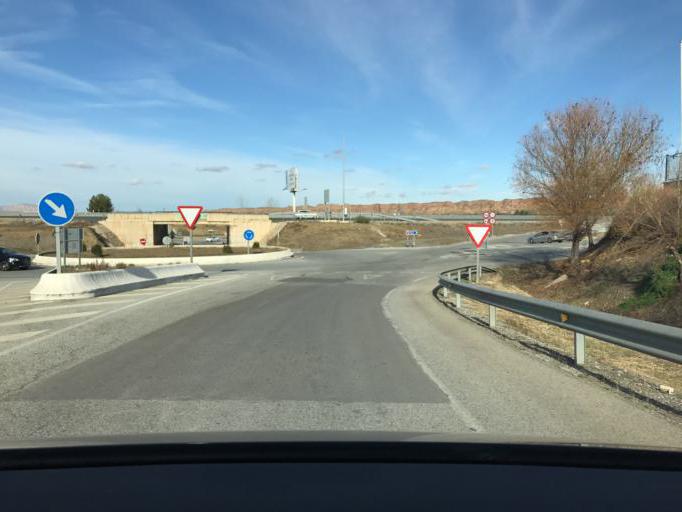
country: ES
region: Andalusia
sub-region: Provincia de Granada
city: Guadix
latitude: 37.3200
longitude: -3.1597
